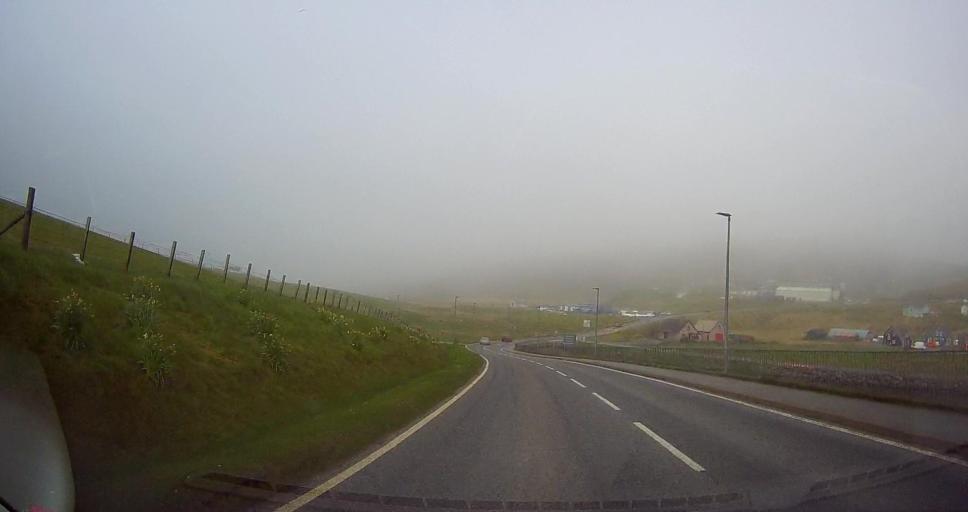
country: GB
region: Scotland
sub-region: Shetland Islands
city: Lerwick
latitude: 60.1411
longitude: -1.2695
